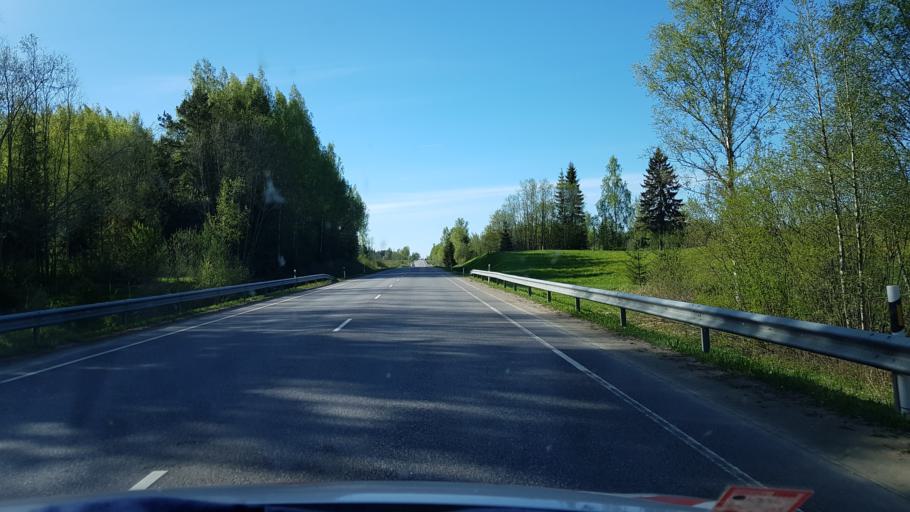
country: EE
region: Tartu
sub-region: UElenurme vald
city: Ulenurme
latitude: 58.1342
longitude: 26.7189
